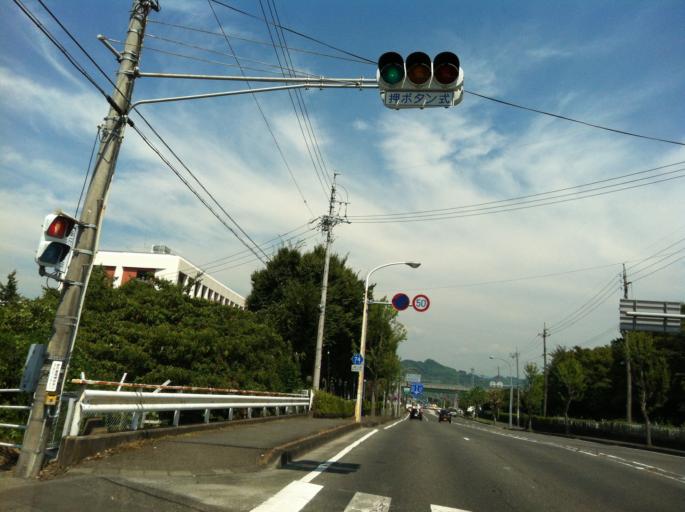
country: JP
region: Shizuoka
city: Shizuoka-shi
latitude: 35.0060
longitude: 138.4039
